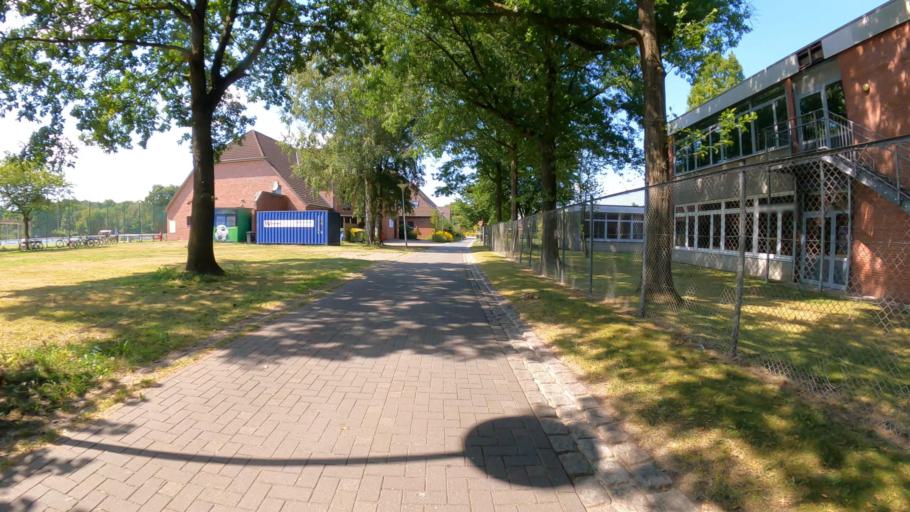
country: DE
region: Schleswig-Holstein
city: Kolln-Reisiek
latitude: 53.7424
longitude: 9.6789
